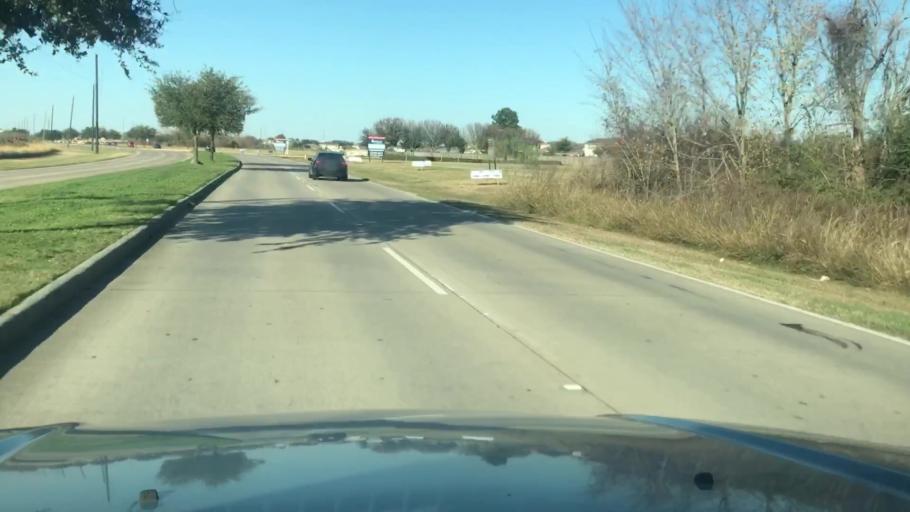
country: US
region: Texas
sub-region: Fort Bend County
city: Cinco Ranch
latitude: 29.8351
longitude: -95.7191
